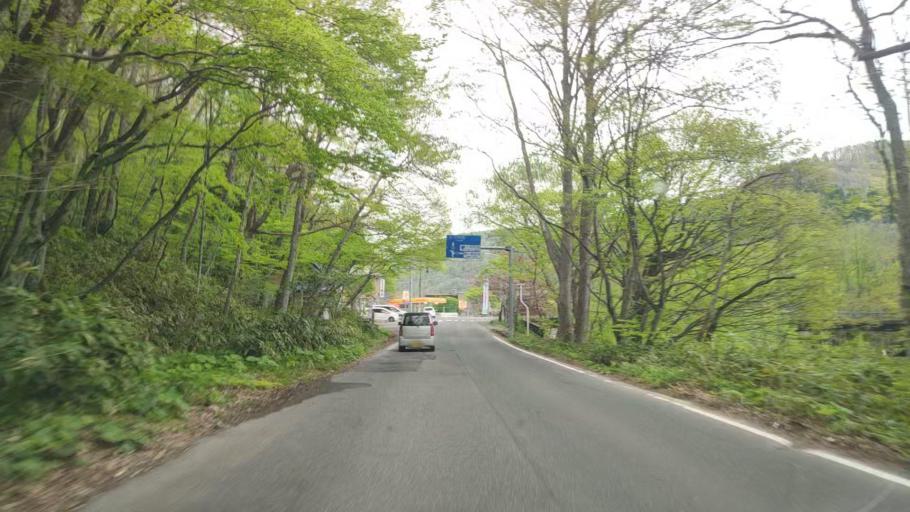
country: JP
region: Aomori
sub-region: Aomori Shi
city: Furudate
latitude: 40.5774
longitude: 140.9852
